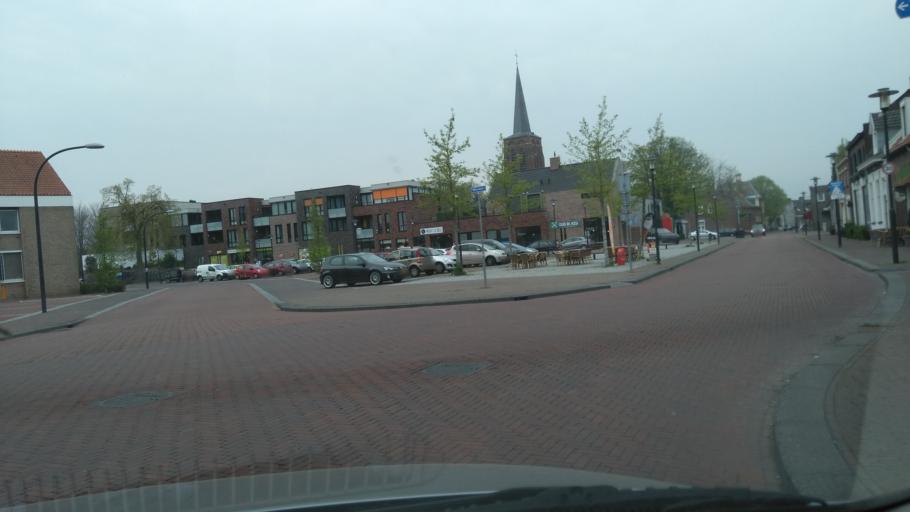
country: NL
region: North Brabant
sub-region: Gemeente Baarle-Nassau
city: Baarle-Nassau
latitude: 51.4827
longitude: 4.9555
